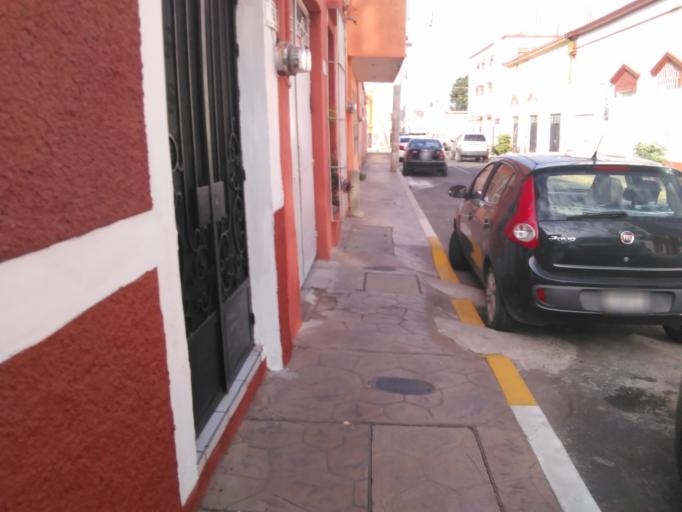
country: MX
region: Nayarit
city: Tepic
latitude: 21.5099
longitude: -104.8889
